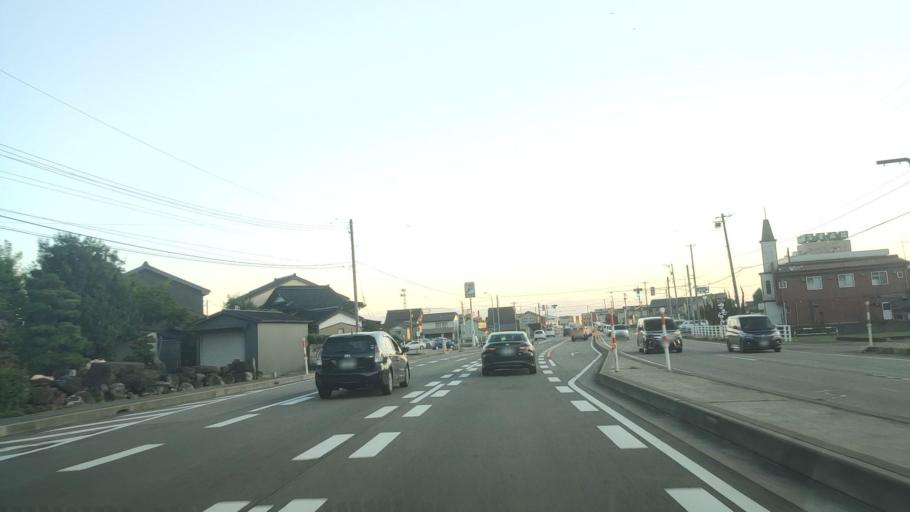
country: JP
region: Toyama
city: Takaoka
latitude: 36.7794
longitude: 137.0002
